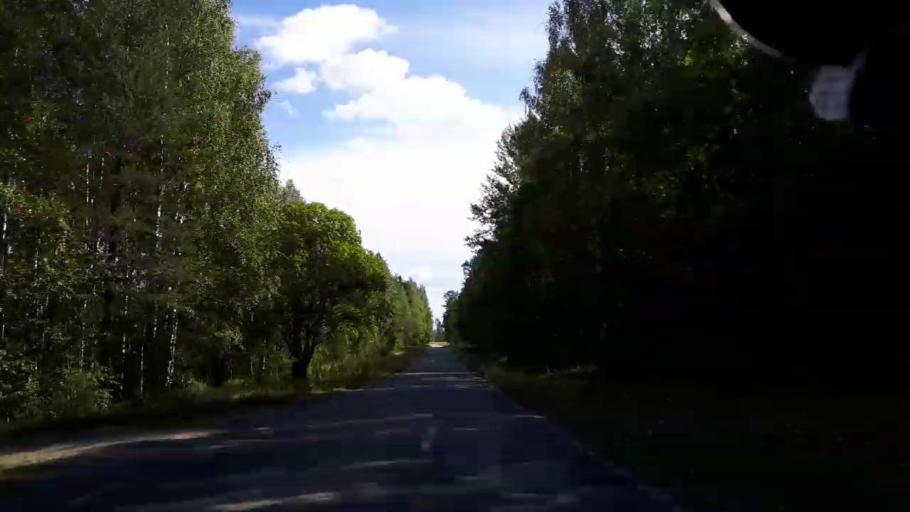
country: SE
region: Jaemtland
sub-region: Braecke Kommun
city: Braecke
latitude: 63.2183
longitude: 15.3249
